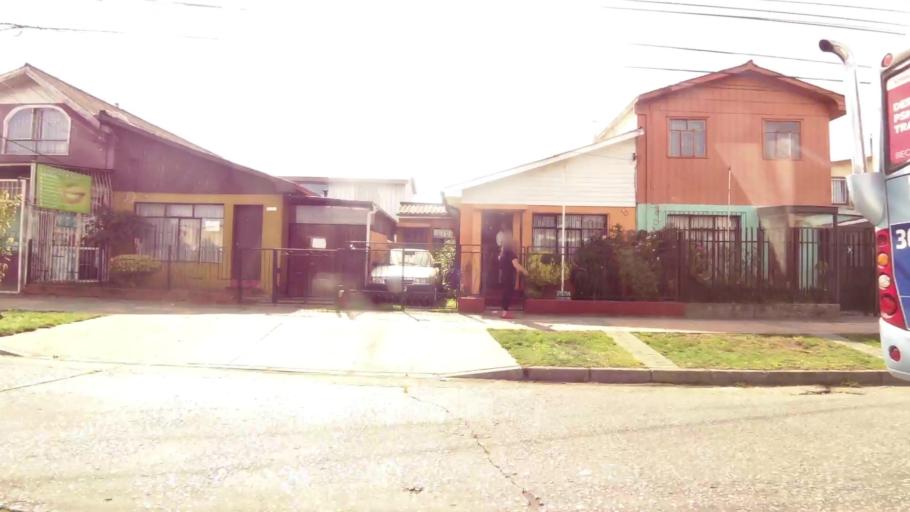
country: CL
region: Biobio
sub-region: Provincia de Concepcion
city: Talcahuano
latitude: -36.7858
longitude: -73.1041
